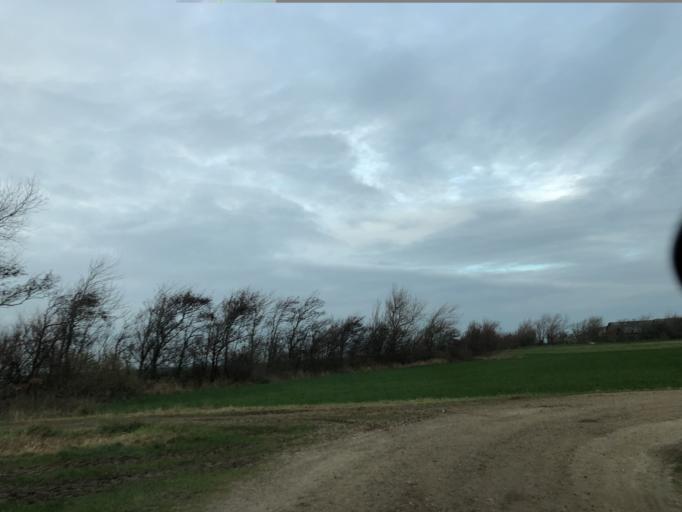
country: DK
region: Central Jutland
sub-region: Holstebro Kommune
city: Ulfborg
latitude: 56.2760
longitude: 8.2175
